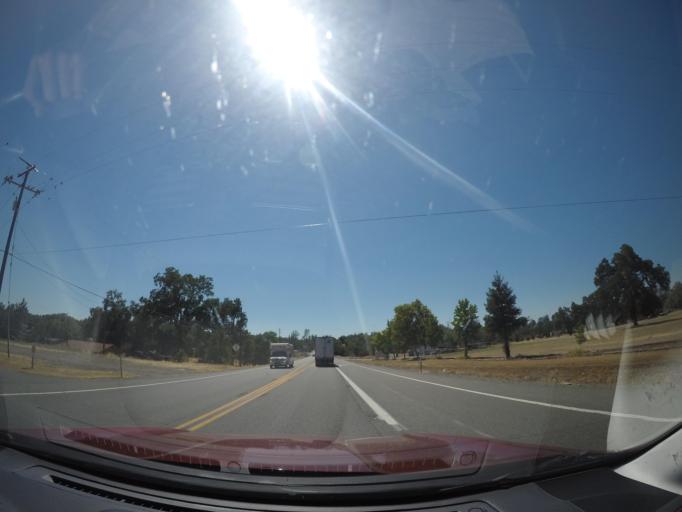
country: US
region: California
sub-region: Shasta County
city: Bella Vista
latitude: 40.6390
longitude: -122.2387
